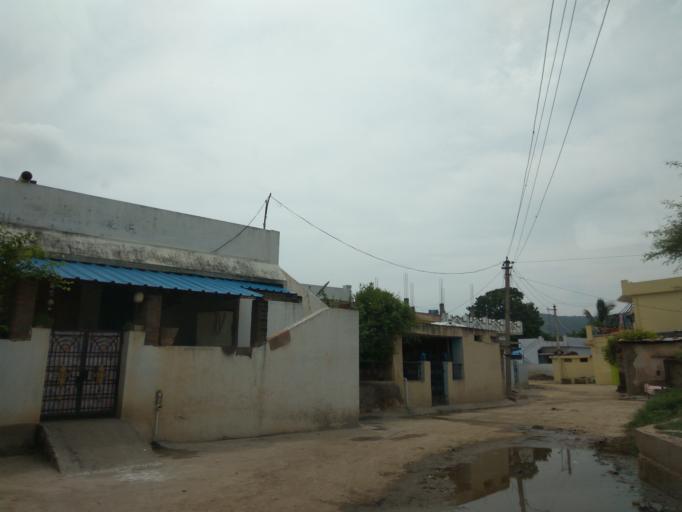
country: IN
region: Andhra Pradesh
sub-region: Prakasam
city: Cumbum
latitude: 15.4555
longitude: 79.0737
